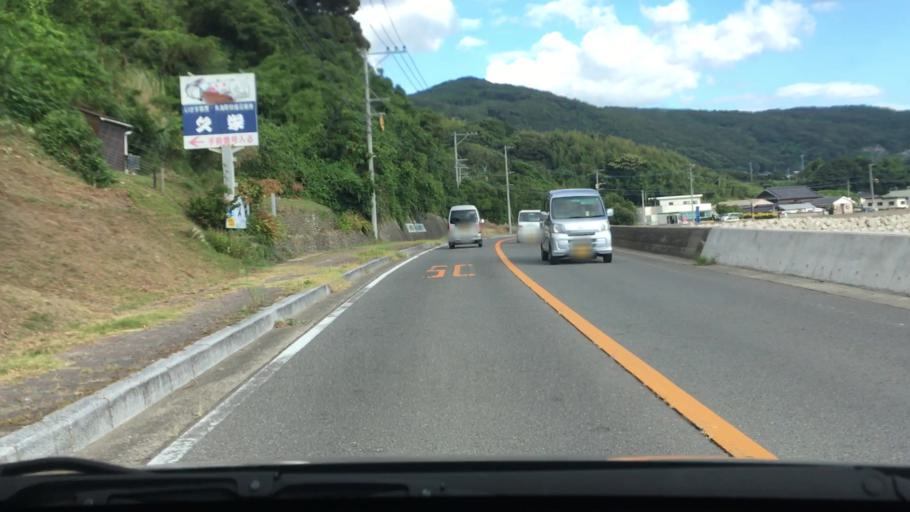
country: JP
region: Nagasaki
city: Togitsu
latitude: 32.8346
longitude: 129.7171
